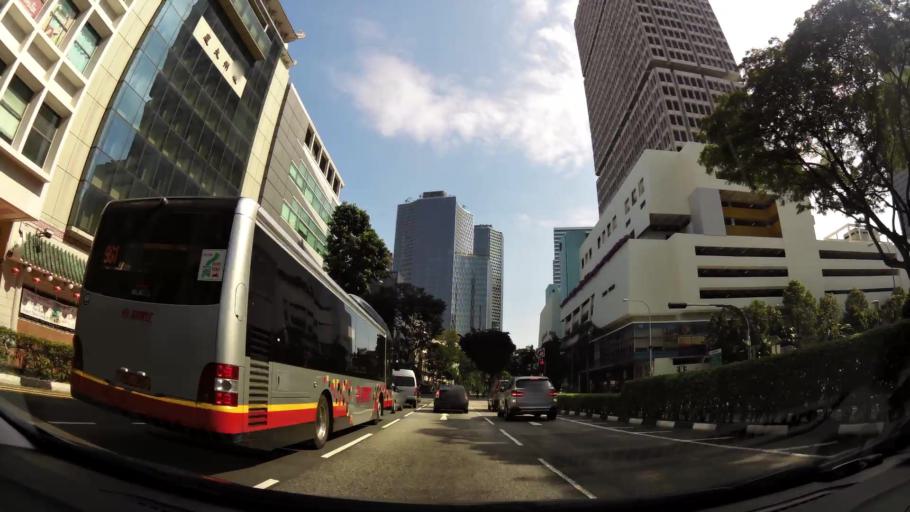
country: SG
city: Singapore
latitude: 1.2962
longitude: 103.8561
